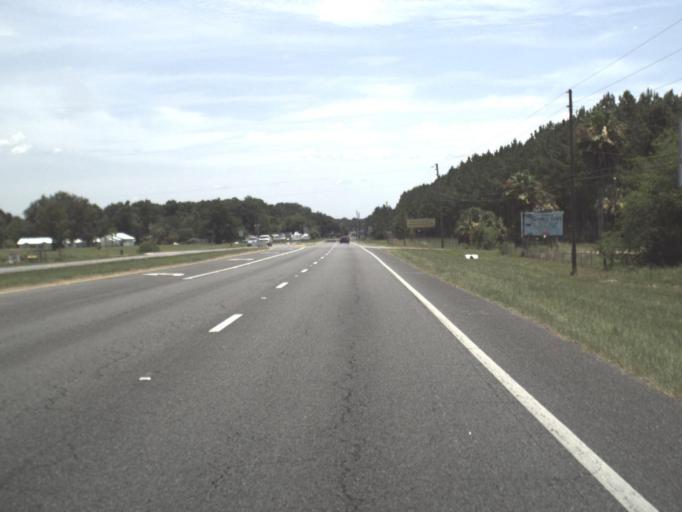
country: US
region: Florida
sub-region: Levy County
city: Manatee Road
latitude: 29.6019
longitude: -82.9923
